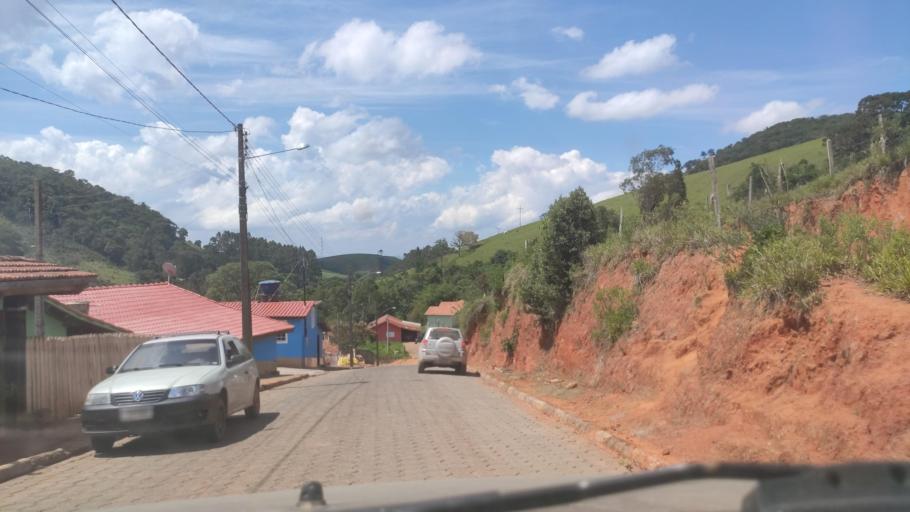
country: BR
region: Minas Gerais
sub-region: Cambui
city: Cambui
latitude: -22.7064
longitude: -46.0340
